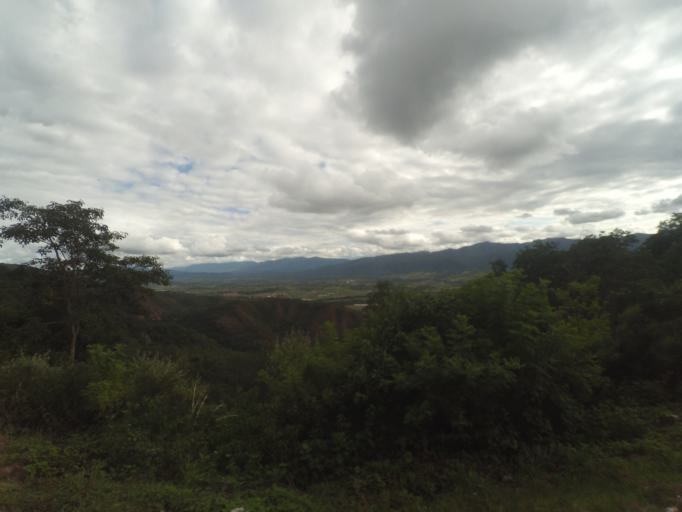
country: BO
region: Santa Cruz
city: Samaipata
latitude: -18.1658
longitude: -63.8908
